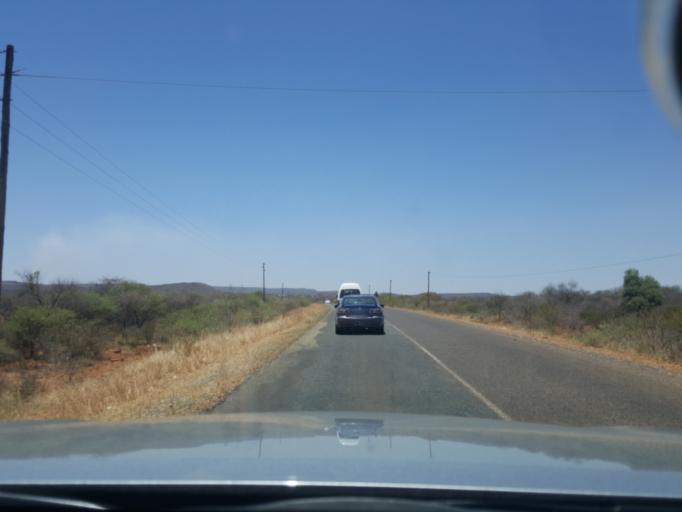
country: ZA
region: North-West
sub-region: Ngaka Modiri Molema District Municipality
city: Zeerust
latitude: -25.3911
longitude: 25.9361
